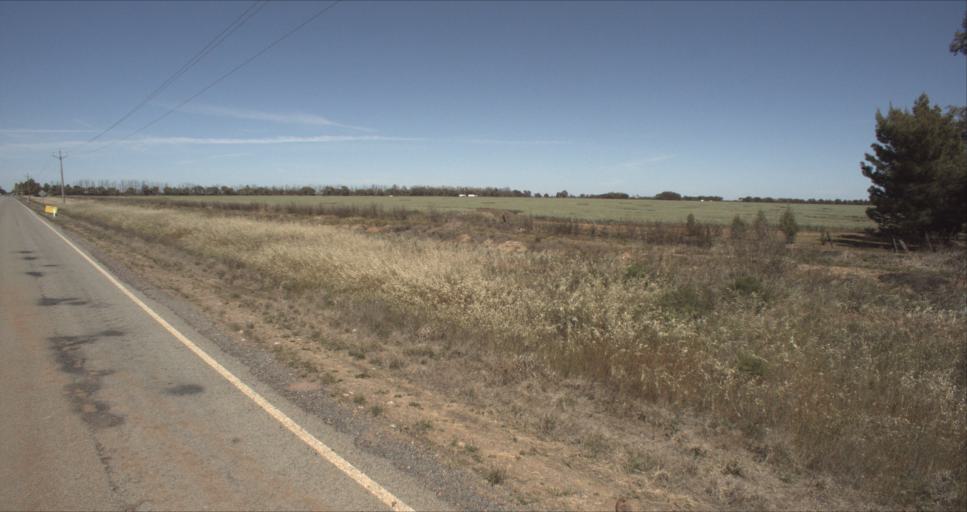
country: AU
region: New South Wales
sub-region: Leeton
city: Leeton
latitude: -34.5143
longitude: 146.2845
